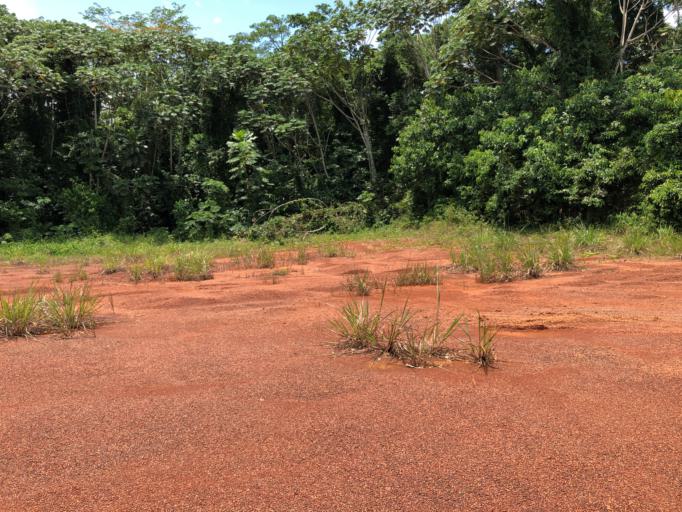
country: CD
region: Eastern Province
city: Kisangani
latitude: 0.4971
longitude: 25.7804
